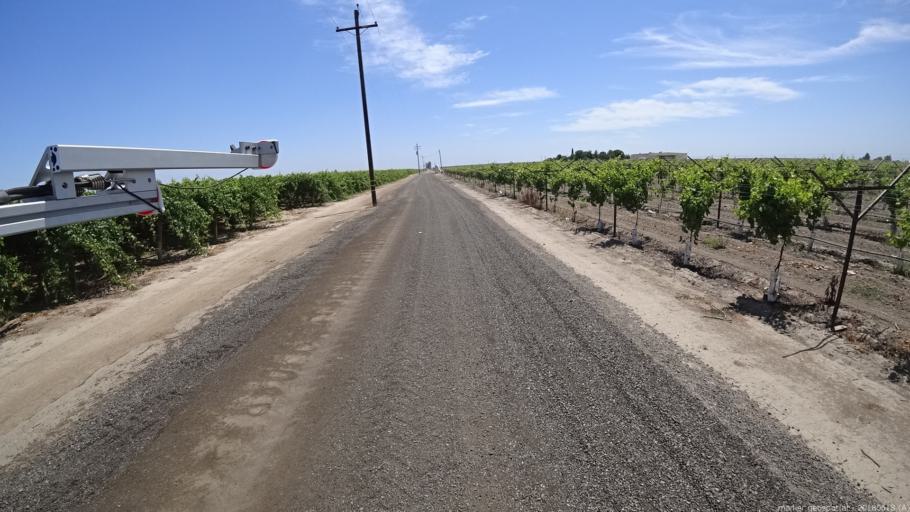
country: US
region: California
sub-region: Madera County
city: Parkwood
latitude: 36.8875
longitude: -120.1347
